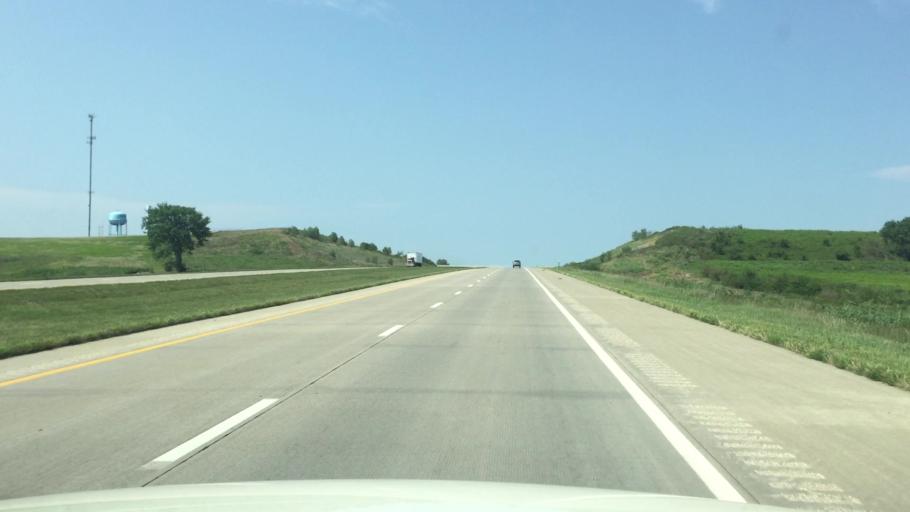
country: US
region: Kansas
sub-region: Linn County
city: Pleasanton
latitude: 38.1035
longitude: -94.7134
